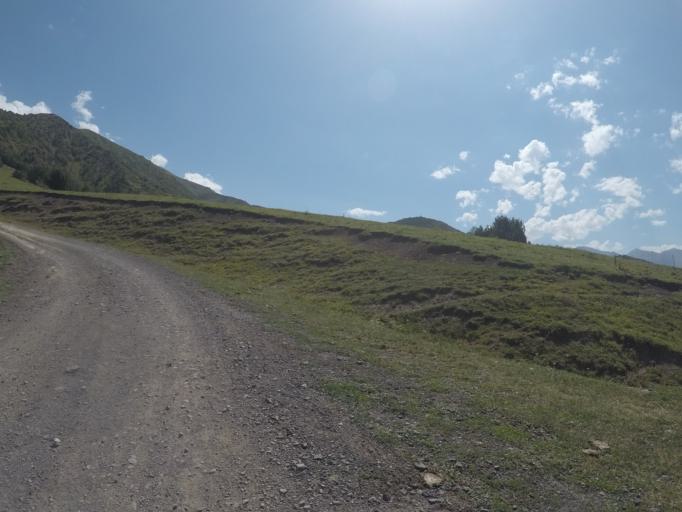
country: KG
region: Chuy
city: Bishkek
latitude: 42.6469
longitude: 74.5582
